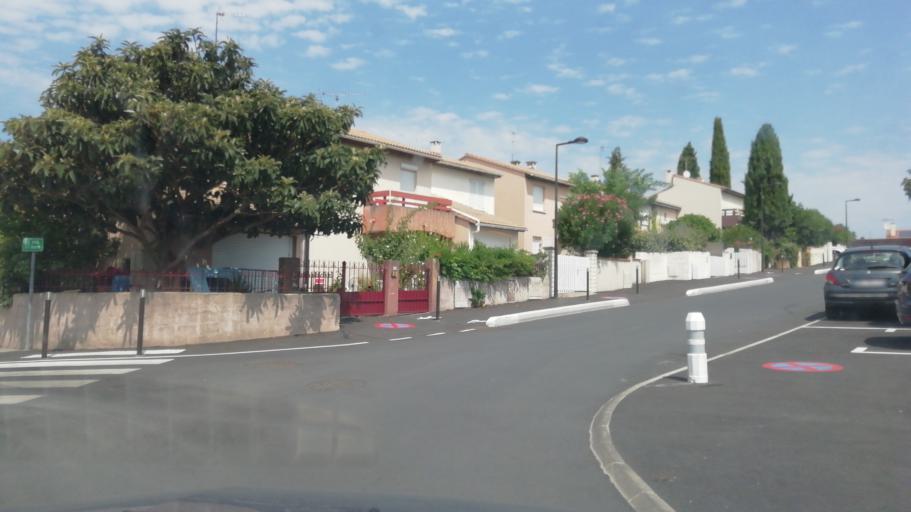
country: FR
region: Languedoc-Roussillon
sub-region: Departement de l'Herault
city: Saint-Mathieu-de-Treviers
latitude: 43.7699
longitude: 3.8621
